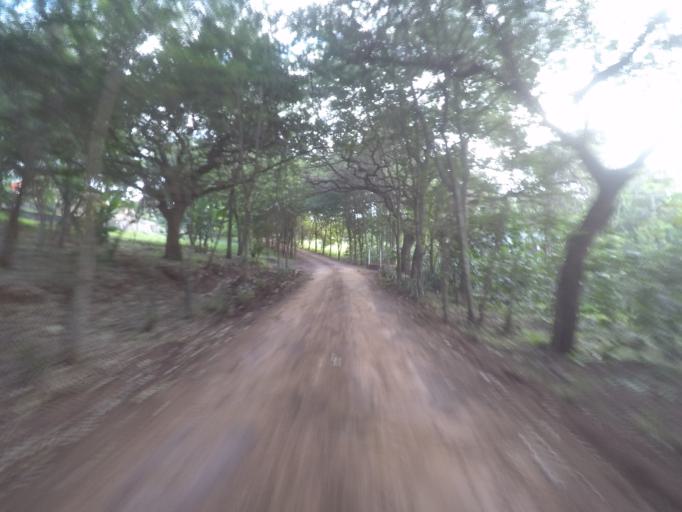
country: TZ
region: Arusha
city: Kiratu
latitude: -3.3216
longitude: 35.6620
